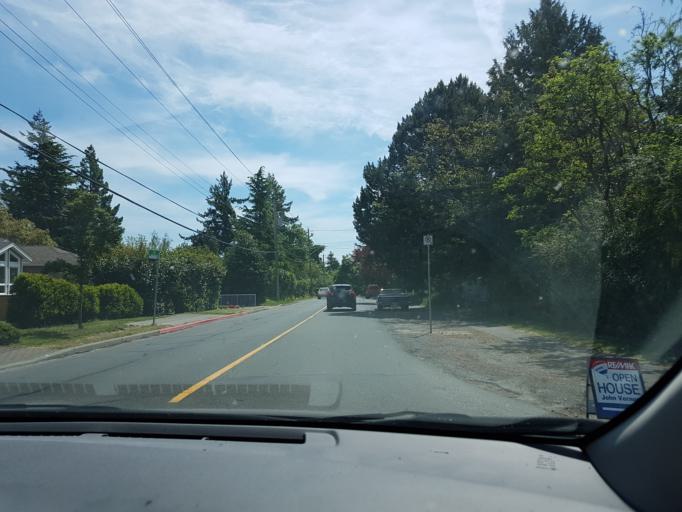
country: CA
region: British Columbia
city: Oak Bay
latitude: 48.4836
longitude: -123.3056
